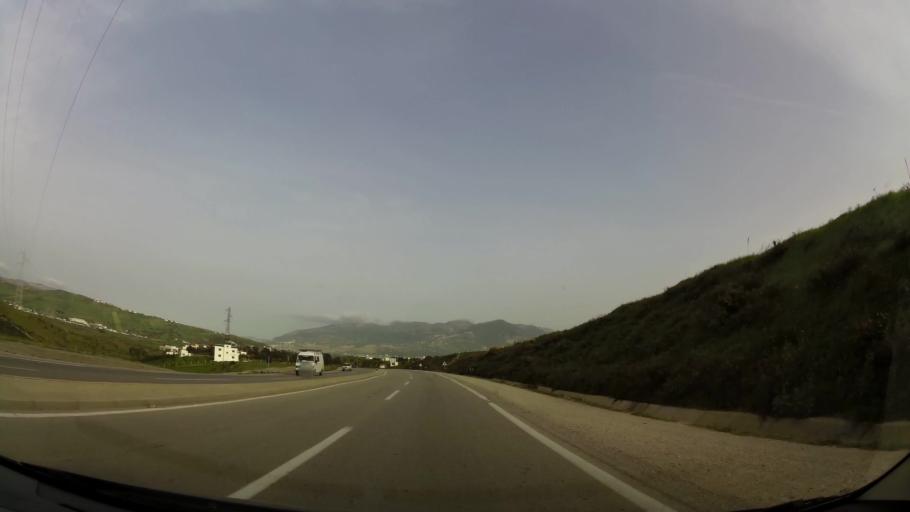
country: MA
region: Tanger-Tetouan
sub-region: Tetouan
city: Saddina
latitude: 35.5623
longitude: -5.4837
